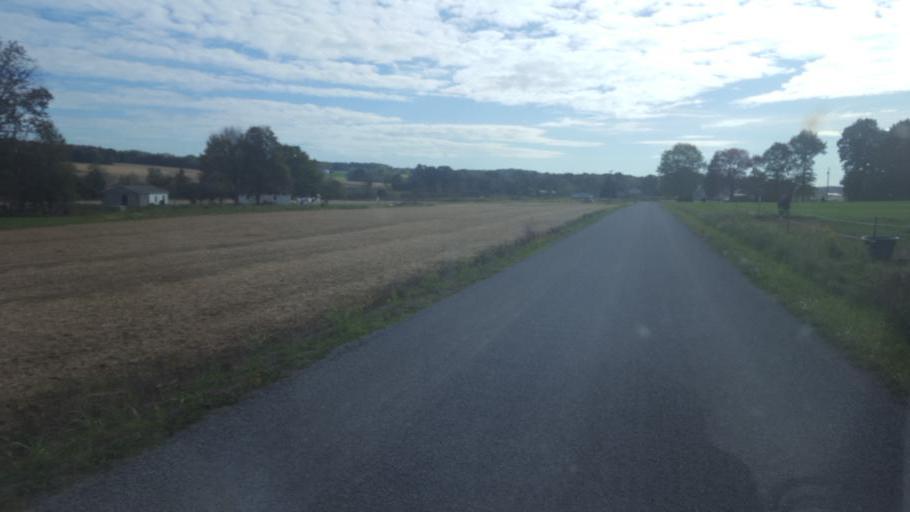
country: US
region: Pennsylvania
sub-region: Mercer County
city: Reynolds Heights
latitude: 41.3350
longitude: -80.3012
